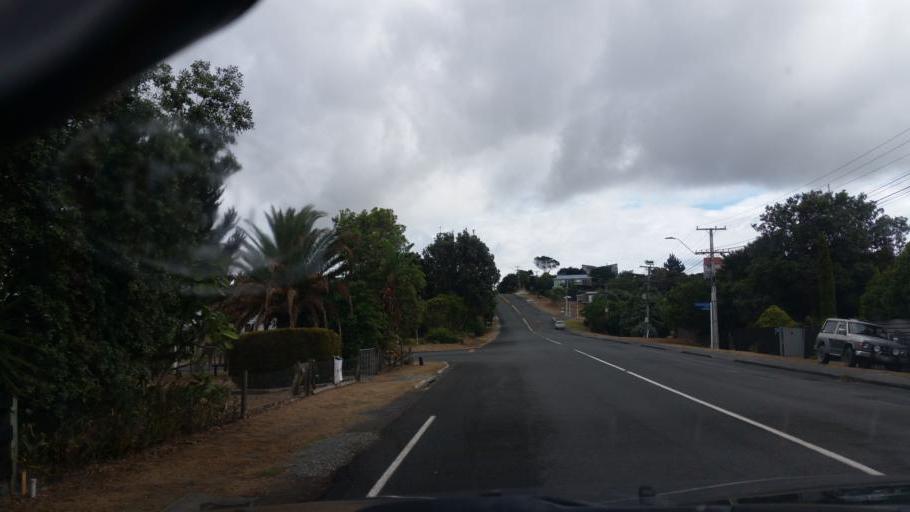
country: NZ
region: Auckland
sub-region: Auckland
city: Wellsford
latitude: -36.0900
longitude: 174.5843
